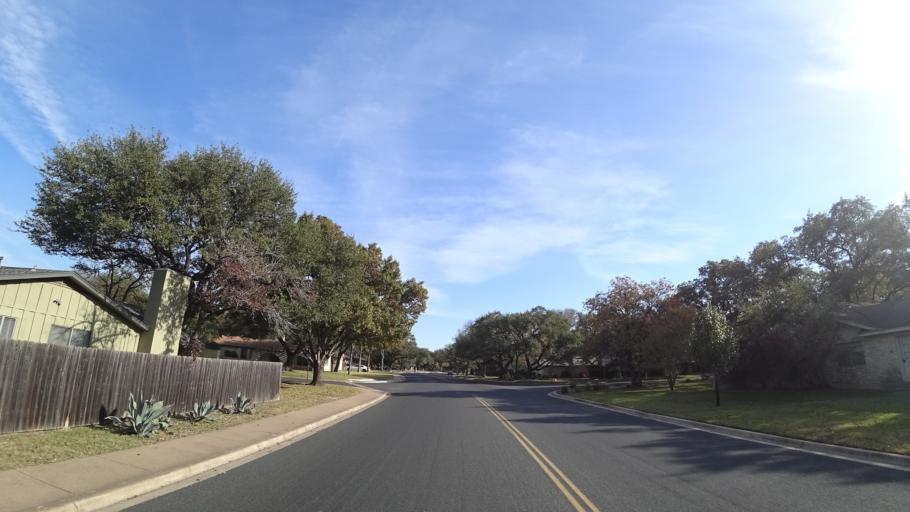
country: US
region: Texas
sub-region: Williamson County
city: Jollyville
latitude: 30.3812
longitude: -97.7522
